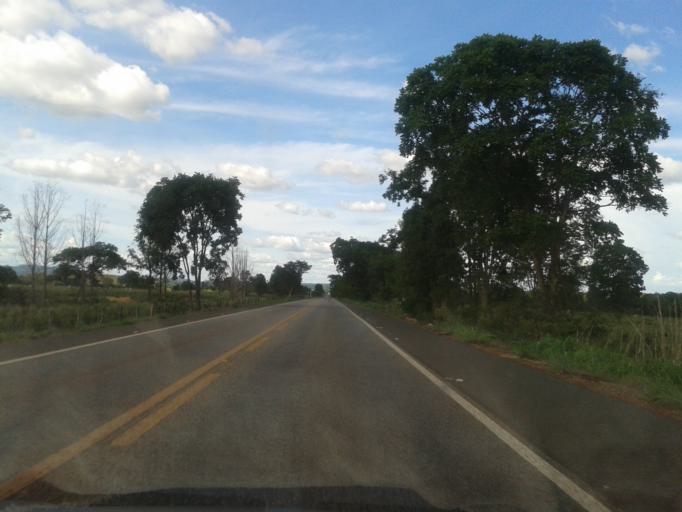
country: BR
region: Goias
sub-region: Mozarlandia
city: Mozarlandia
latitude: -15.0282
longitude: -50.6001
